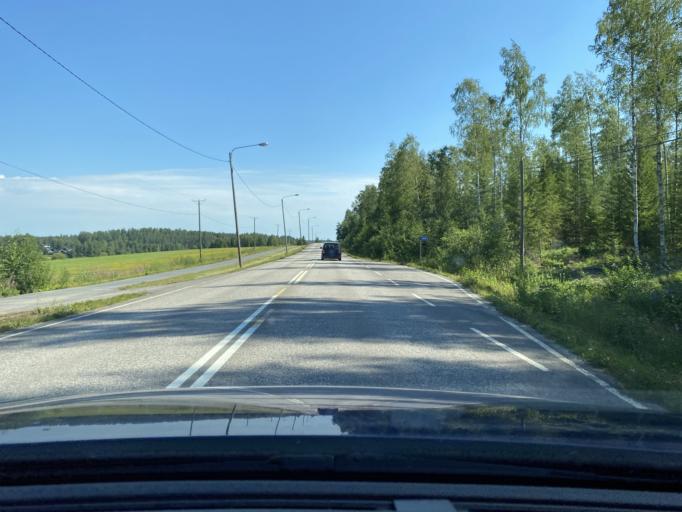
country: FI
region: Central Finland
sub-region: Jaemsae
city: Jaemsae
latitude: 61.8895
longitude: 25.3062
